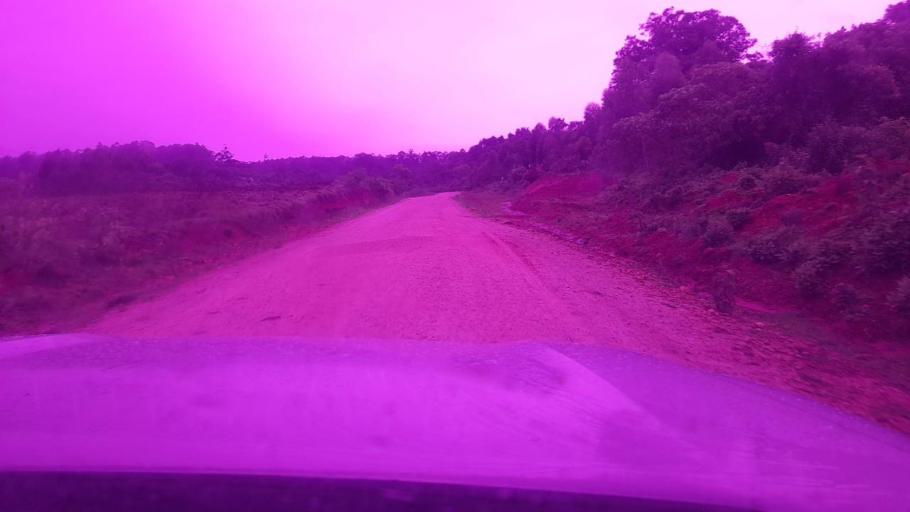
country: ET
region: Southern Nations, Nationalities, and People's Region
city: Bonga
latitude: 7.4438
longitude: 36.1542
